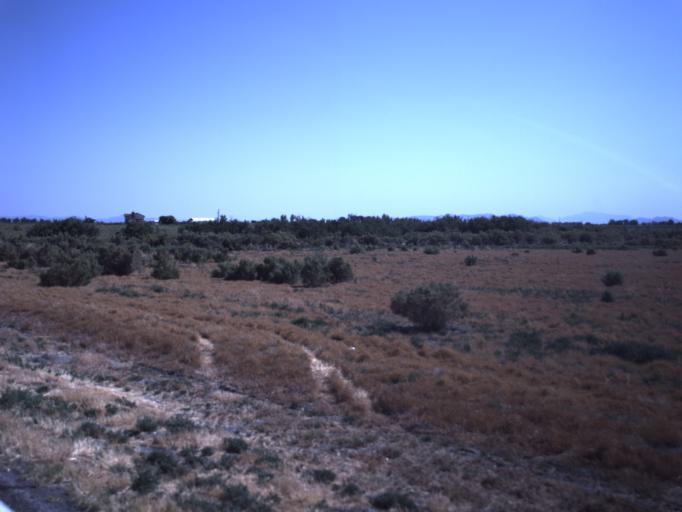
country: US
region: Utah
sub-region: Millard County
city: Delta
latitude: 39.3045
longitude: -112.6525
